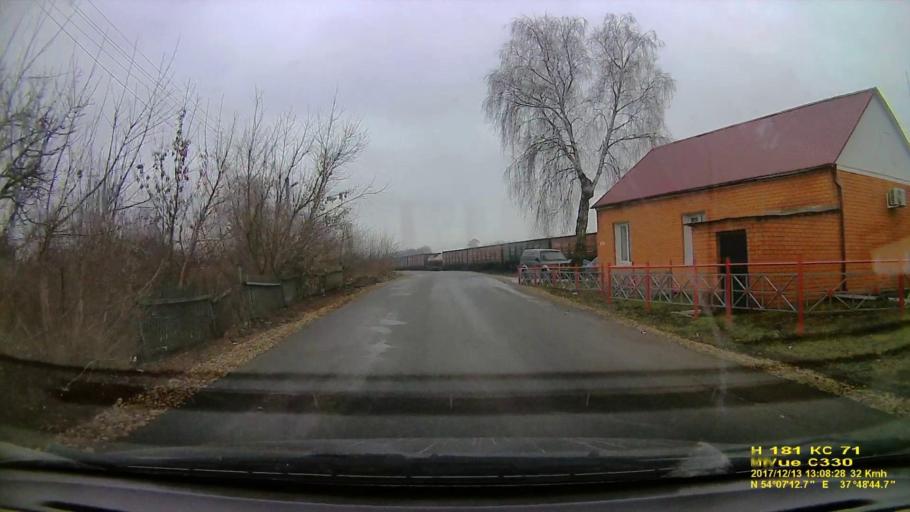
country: RU
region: Tula
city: Bolokhovo
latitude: 54.1201
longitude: 37.8126
